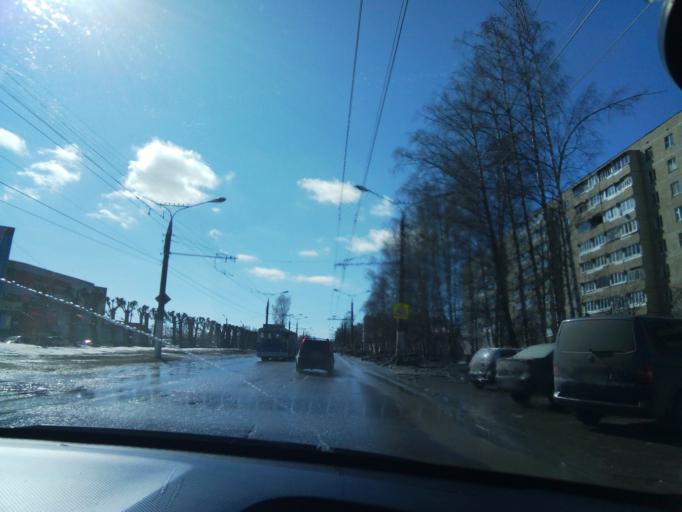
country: RU
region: Chuvashia
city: Novyye Lapsary
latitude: 56.1121
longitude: 47.1839
